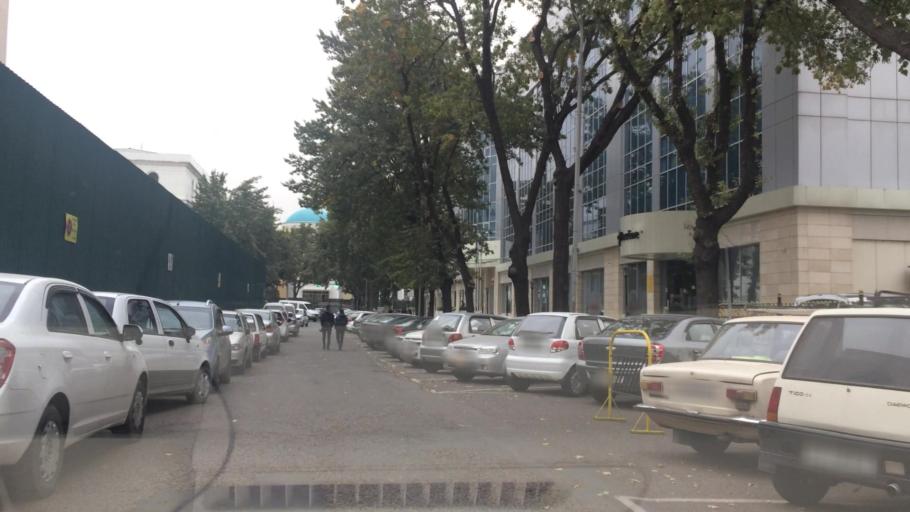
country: UZ
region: Toshkent Shahri
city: Tashkent
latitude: 41.3087
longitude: 69.2769
